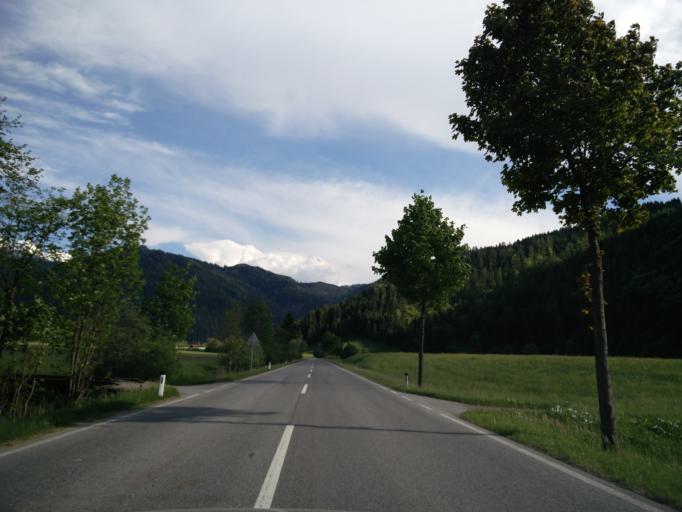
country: AT
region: Tyrol
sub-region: Politischer Bezirk Kitzbuhel
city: Kirchdorf in Tirol
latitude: 47.5894
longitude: 12.4704
